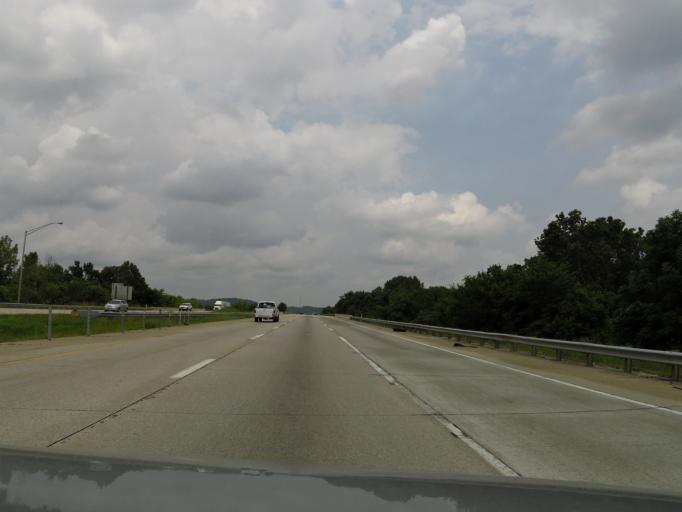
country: US
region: Kentucky
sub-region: Bullitt County
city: Shepherdsville
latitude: 37.9313
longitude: -85.6878
